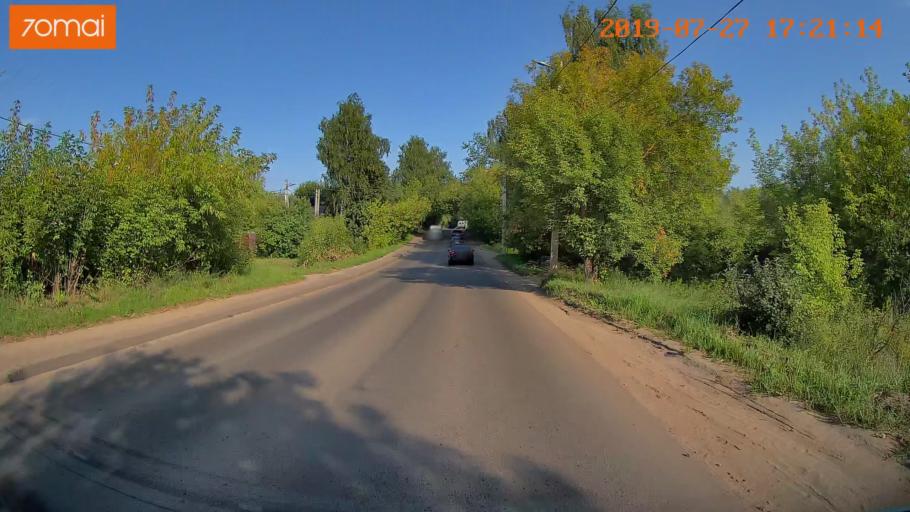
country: RU
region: Ivanovo
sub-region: Gorod Ivanovo
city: Ivanovo
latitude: 57.0278
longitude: 40.9311
